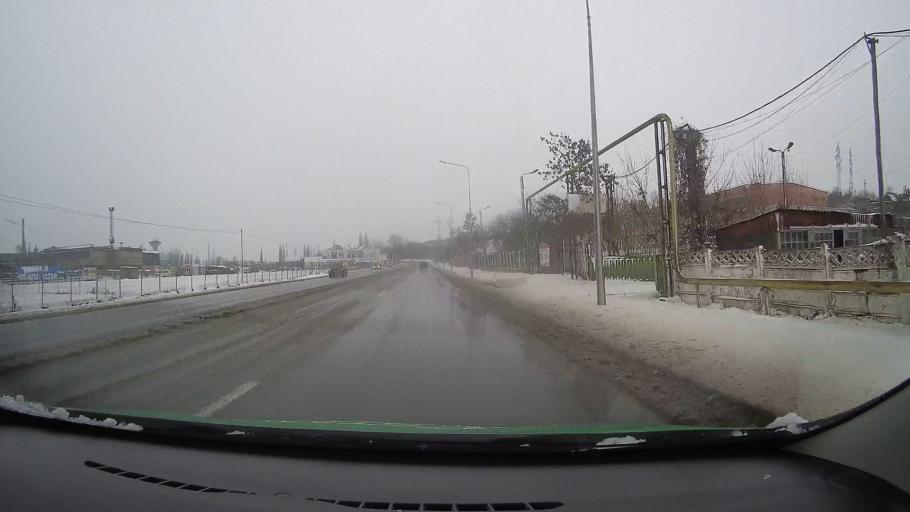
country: RO
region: Hunedoara
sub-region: Municipiul Hunedoara
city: Pestisu Mare
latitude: 45.7894
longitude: 22.9144
